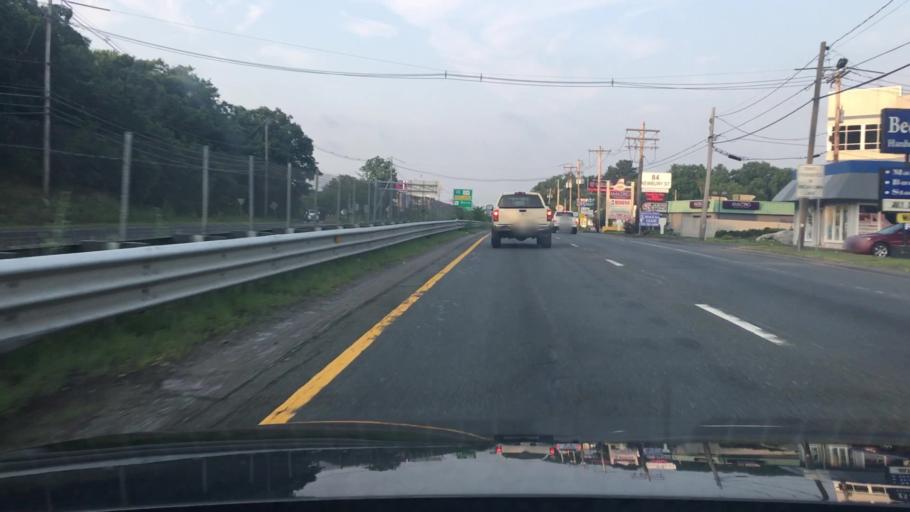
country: US
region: Massachusetts
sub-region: Essex County
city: South Peabody
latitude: 42.5316
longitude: -70.9918
